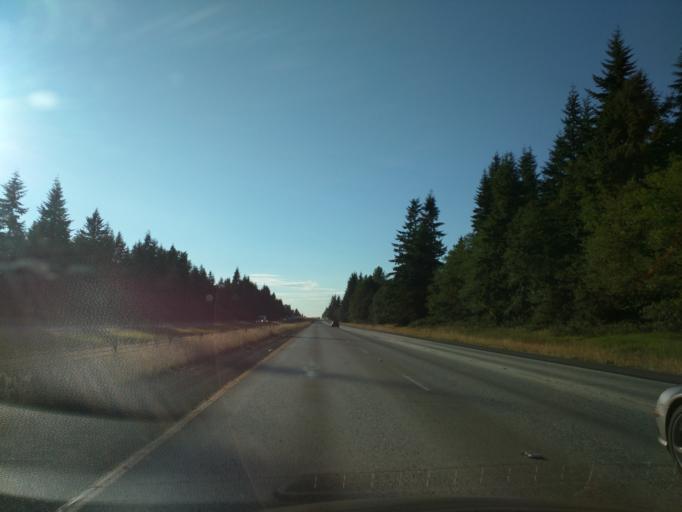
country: US
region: Washington
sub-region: Snohomish County
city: Stanwood
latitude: 48.2832
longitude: -122.2867
